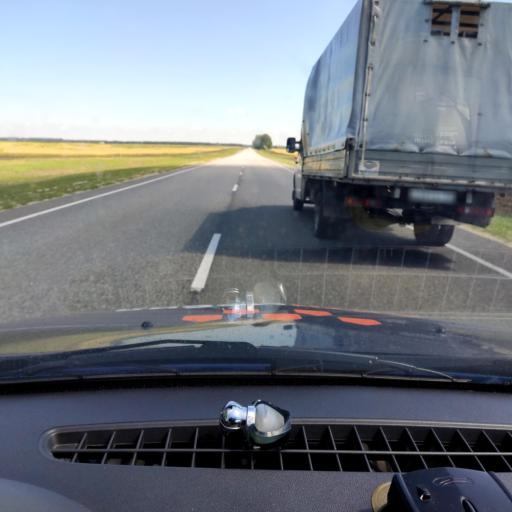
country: RU
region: Orjol
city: Pokrovskoye
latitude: 52.6371
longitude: 36.6835
